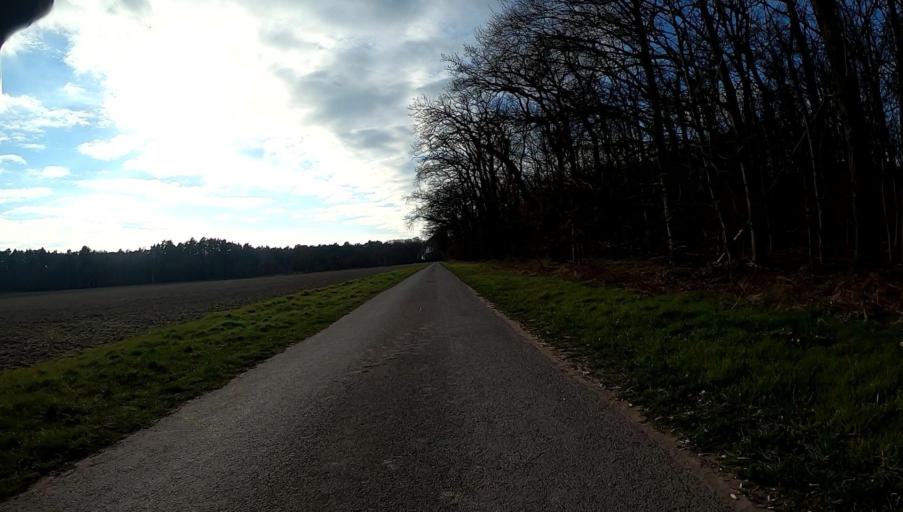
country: DE
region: Lower Saxony
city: Schwarmstedt
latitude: 52.6189
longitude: 9.6178
